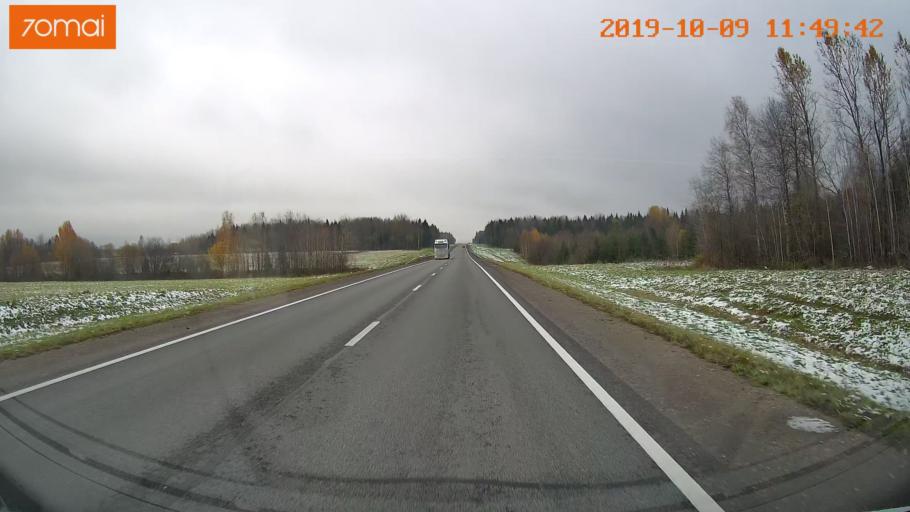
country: RU
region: Vologda
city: Gryazovets
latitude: 58.8152
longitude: 40.2342
